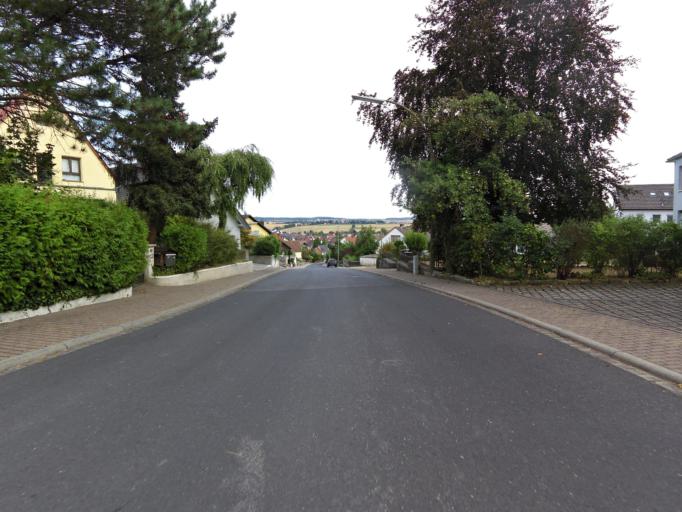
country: DE
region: Bavaria
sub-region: Regierungsbezirk Unterfranken
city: Hettstadt
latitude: 49.8022
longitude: 9.8086
